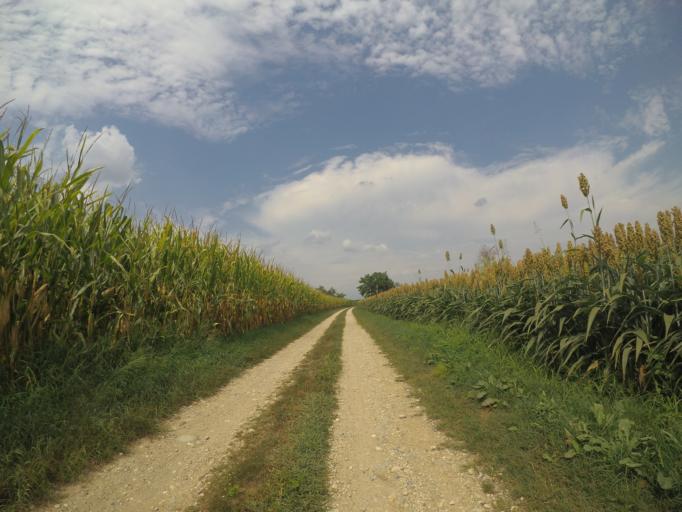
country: IT
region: Friuli Venezia Giulia
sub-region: Provincia di Udine
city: Bertiolo
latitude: 45.9631
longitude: 13.0678
